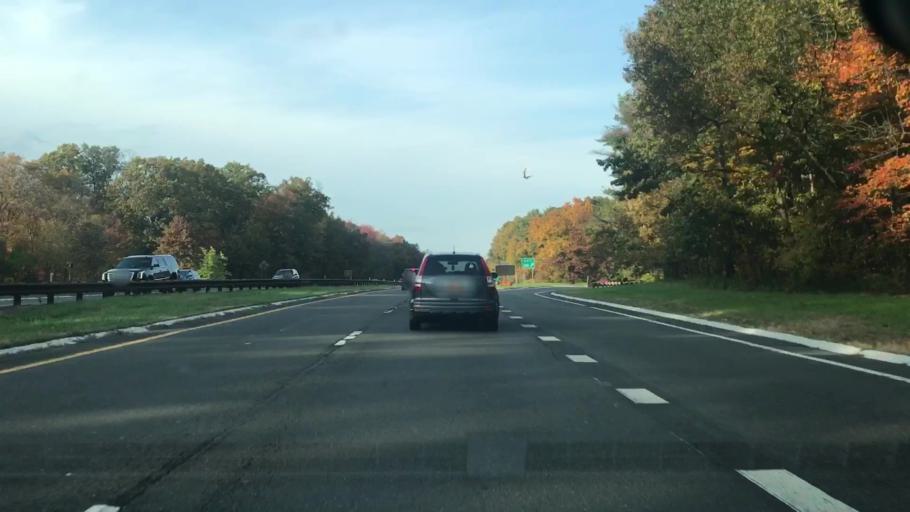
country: US
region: New York
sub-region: Rockland County
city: West Nyack
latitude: 41.0914
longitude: -73.9906
